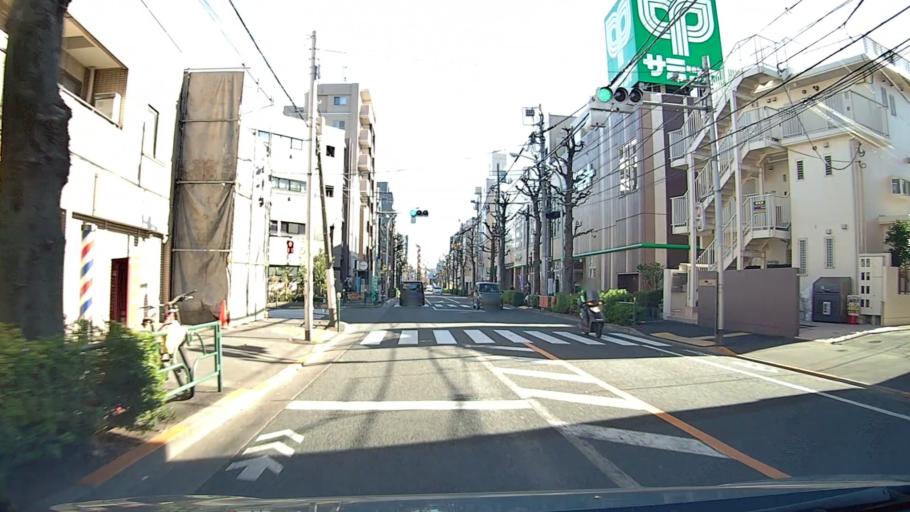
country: JP
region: Tokyo
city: Tokyo
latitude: 35.7242
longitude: 139.6468
